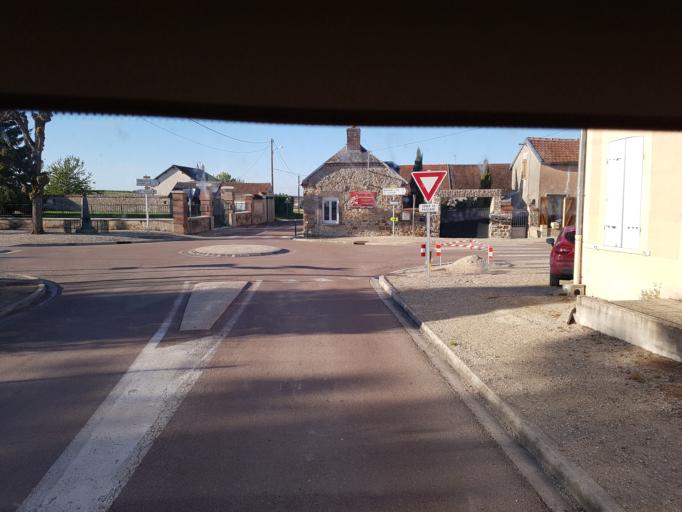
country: FR
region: Champagne-Ardenne
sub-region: Departement de l'Aube
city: Marigny-le-Chatel
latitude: 48.3890
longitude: 3.6544
